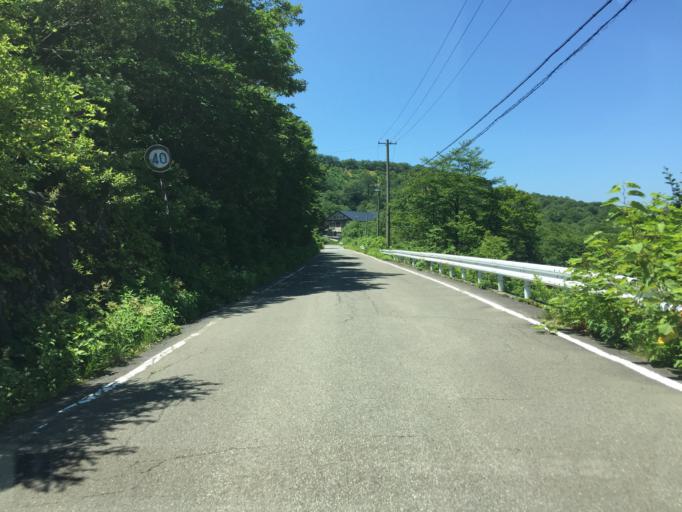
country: JP
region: Fukushima
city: Inawashiro
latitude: 37.6701
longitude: 140.2635
